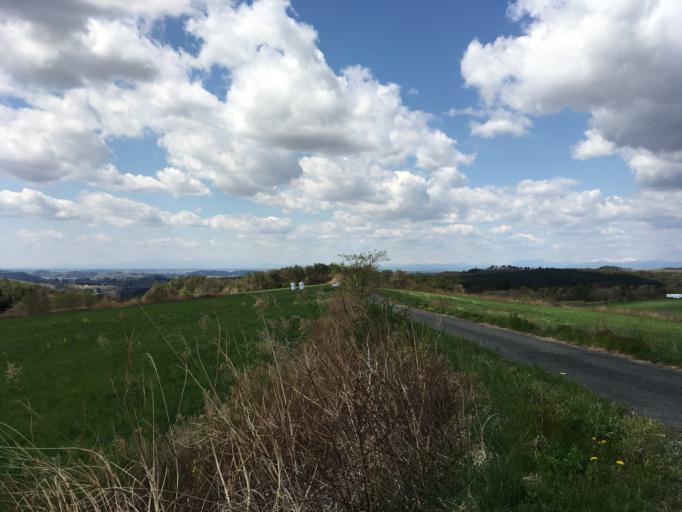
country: JP
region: Iwate
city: Ichinoseki
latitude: 38.8067
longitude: 141.2599
